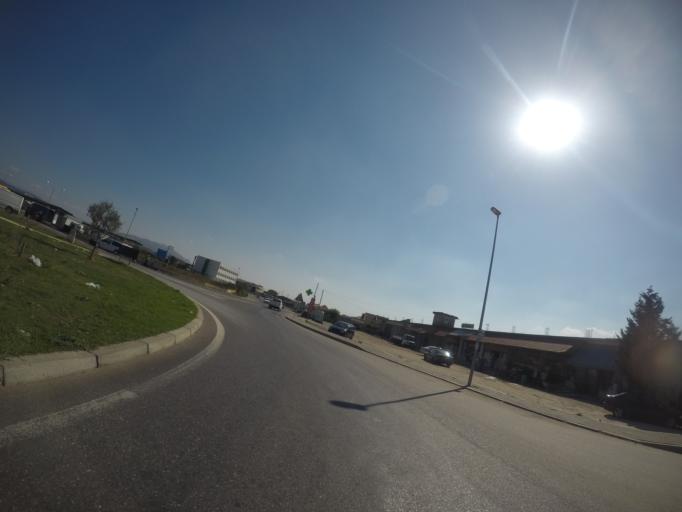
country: AL
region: Shkoder
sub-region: Rrethi i Shkodres
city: Shkoder
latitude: 42.0892
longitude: 19.5072
